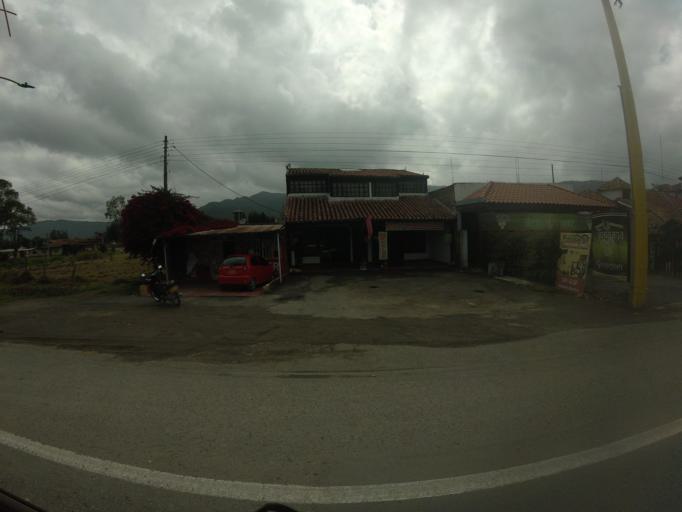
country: CO
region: Boyaca
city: Tibasosa
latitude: 5.7839
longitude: -72.9828
